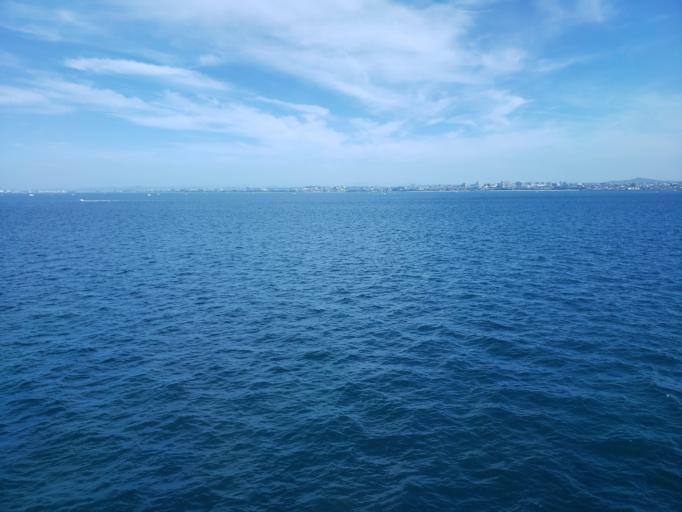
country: JP
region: Hyogo
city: Akashi
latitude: 34.6212
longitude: 134.9586
